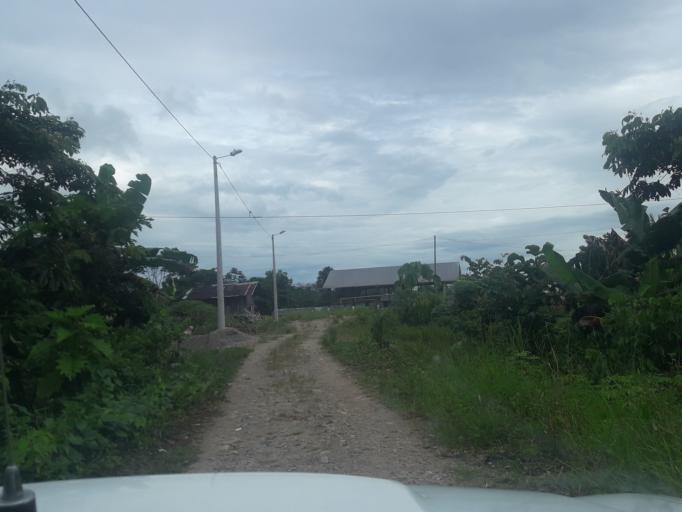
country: EC
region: Napo
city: Tena
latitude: -0.9545
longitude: -77.8155
